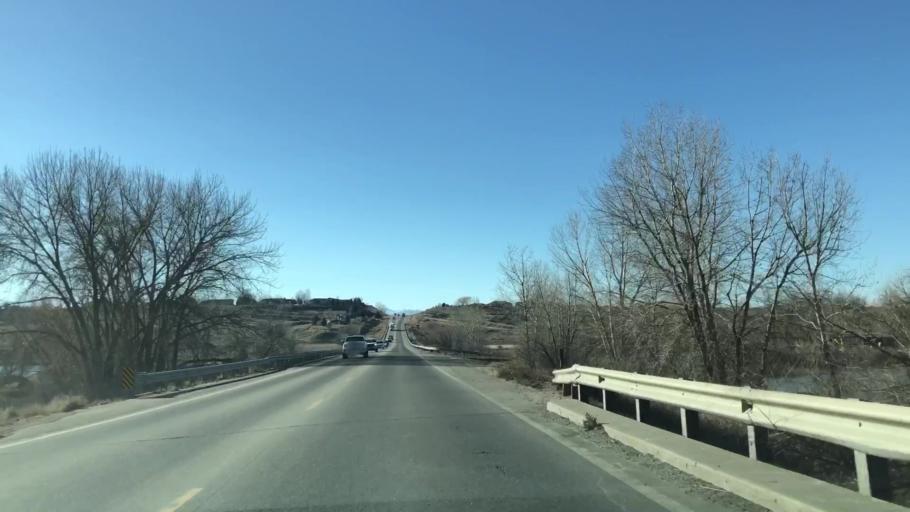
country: US
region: Colorado
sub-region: Weld County
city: Windsor
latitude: 40.4794
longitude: -104.9539
